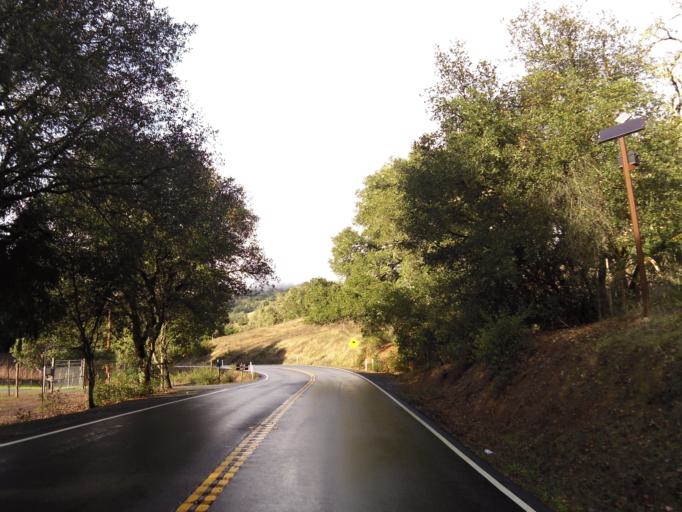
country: US
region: California
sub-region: Sonoma County
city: Cloverdale
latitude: 38.8816
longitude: -123.1156
